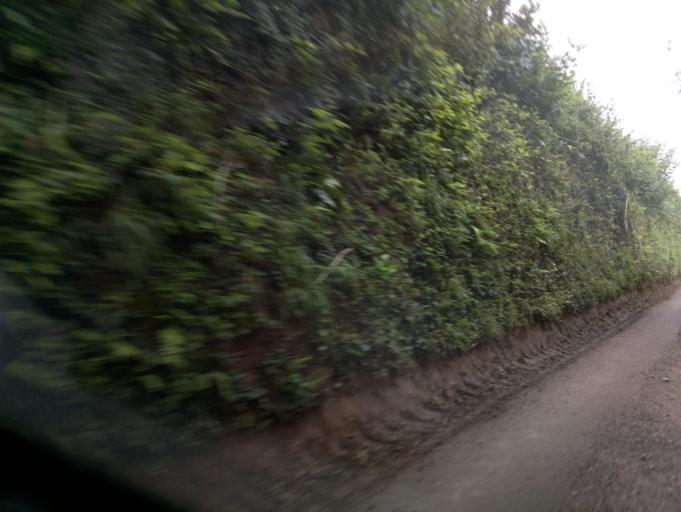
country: GB
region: England
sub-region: Devon
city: Kingsbridge
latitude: 50.2936
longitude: -3.7174
